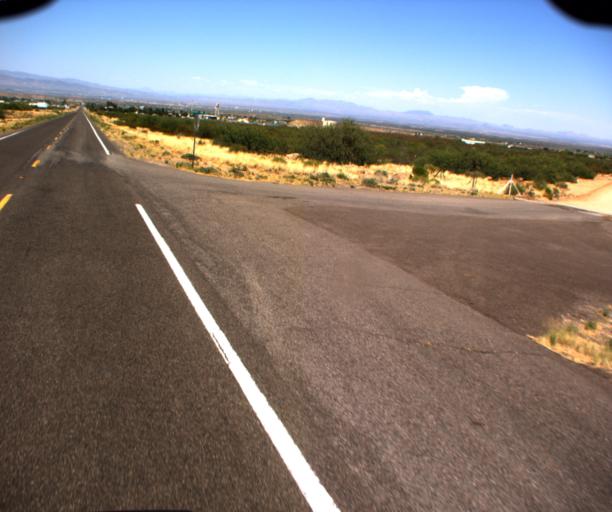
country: US
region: Arizona
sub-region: Graham County
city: Swift Trail Junction
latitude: 32.7101
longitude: -109.7341
